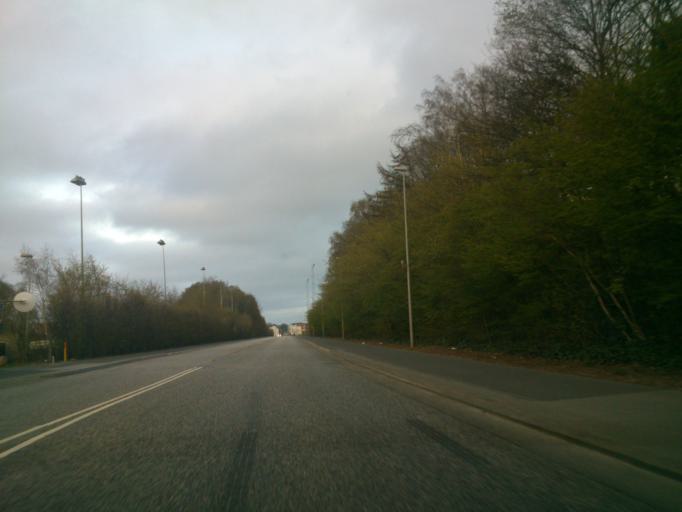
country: DK
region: South Denmark
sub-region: Fredericia Kommune
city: Fredericia
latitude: 55.5618
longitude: 9.7433
